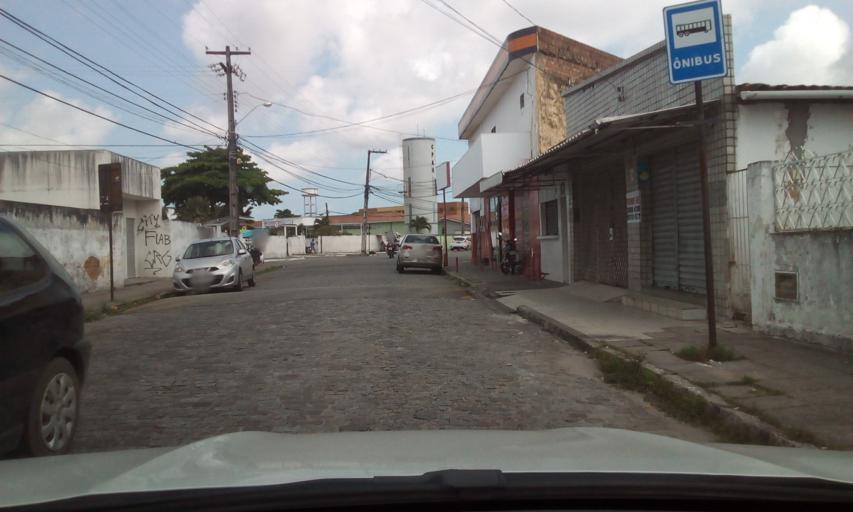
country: BR
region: Paraiba
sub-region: Joao Pessoa
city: Joao Pessoa
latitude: -7.1288
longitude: -34.8762
